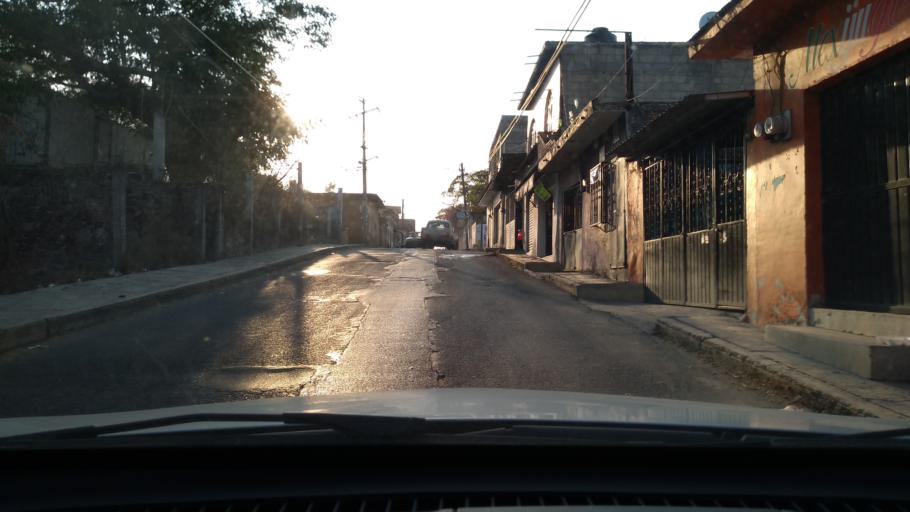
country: MX
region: Morelos
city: Puente de Ixtla
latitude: 18.6226
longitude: -99.3205
